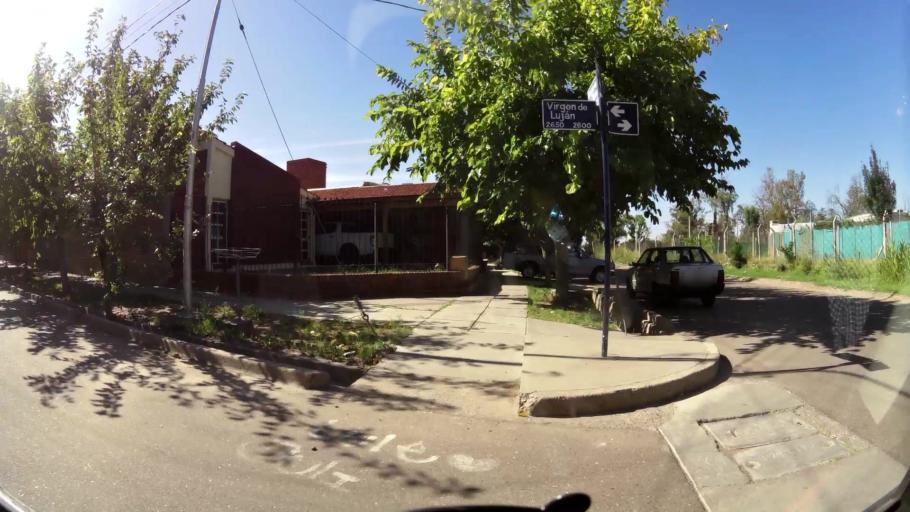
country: AR
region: Mendoza
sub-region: Departamento de Godoy Cruz
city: Godoy Cruz
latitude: -32.9470
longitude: -68.8107
